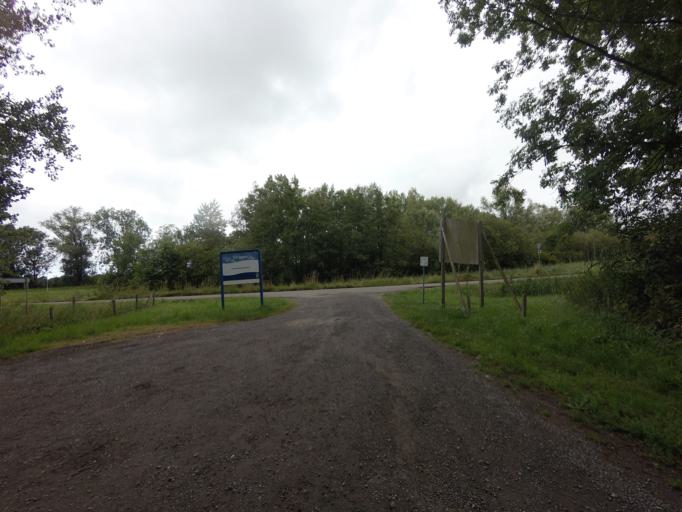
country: NL
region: North Holland
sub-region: Gemeente Velsen
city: Velsen-Zuid
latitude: 52.4257
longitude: 4.7089
